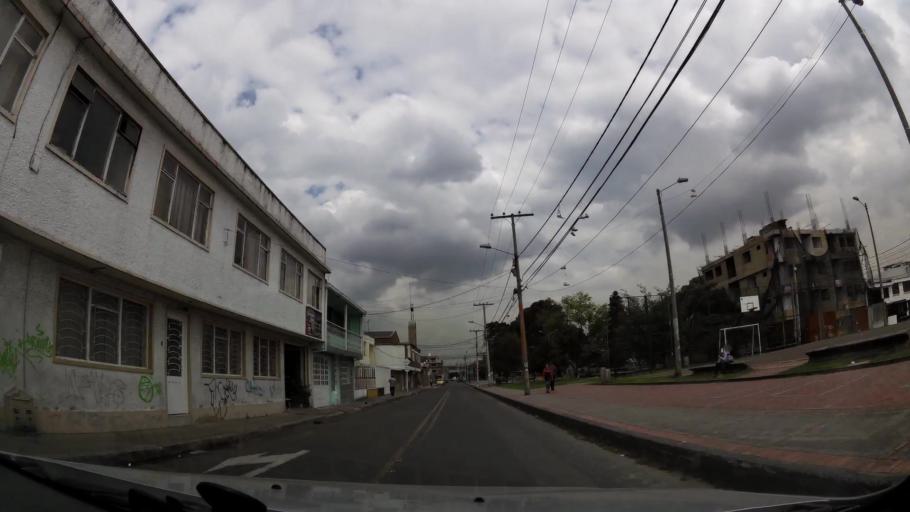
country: CO
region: Bogota D.C.
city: Bogota
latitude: 4.5991
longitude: -74.1006
